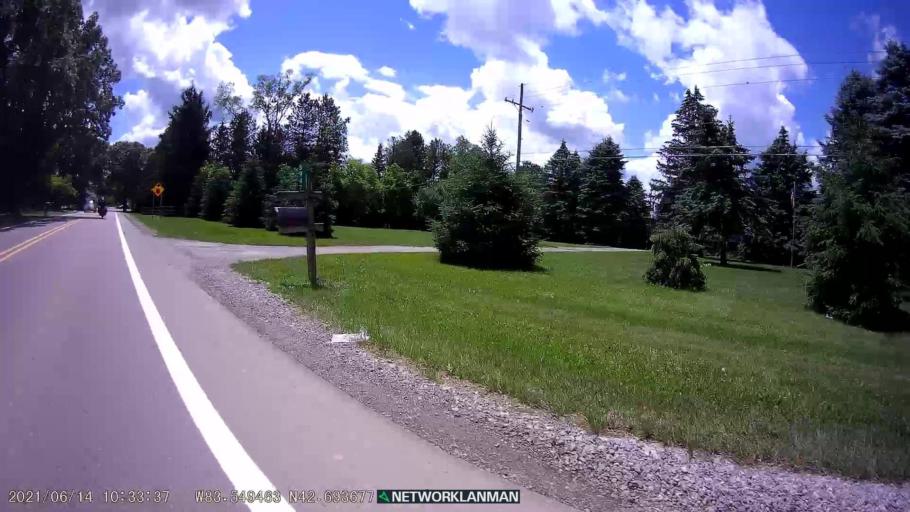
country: US
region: Michigan
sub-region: Oakland County
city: Milford
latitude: 42.6934
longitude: -83.5495
